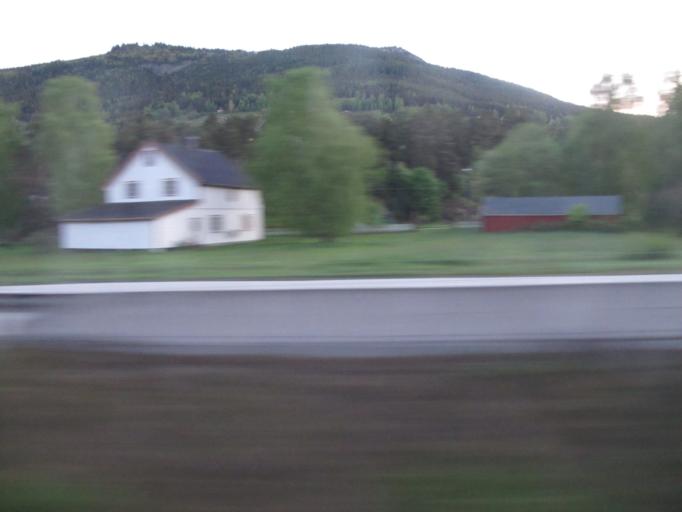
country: NO
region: Oppland
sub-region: Ringebu
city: Ringebu
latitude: 61.5485
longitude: 10.0453
